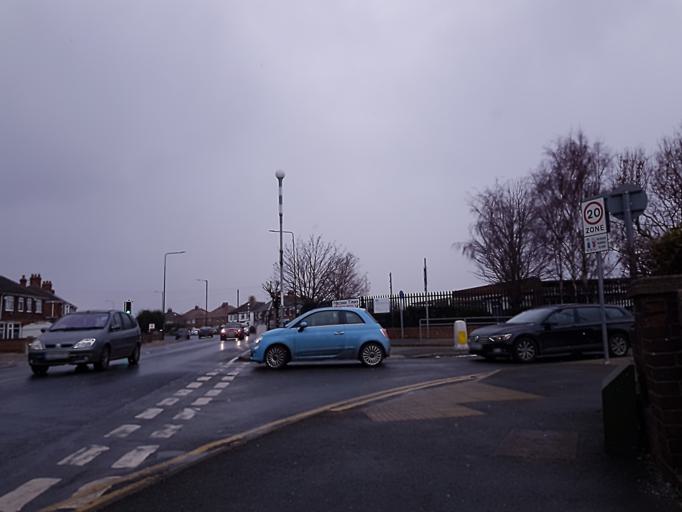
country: GB
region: England
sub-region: North East Lincolnshire
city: Grimbsy
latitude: 53.5623
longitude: -0.1147
